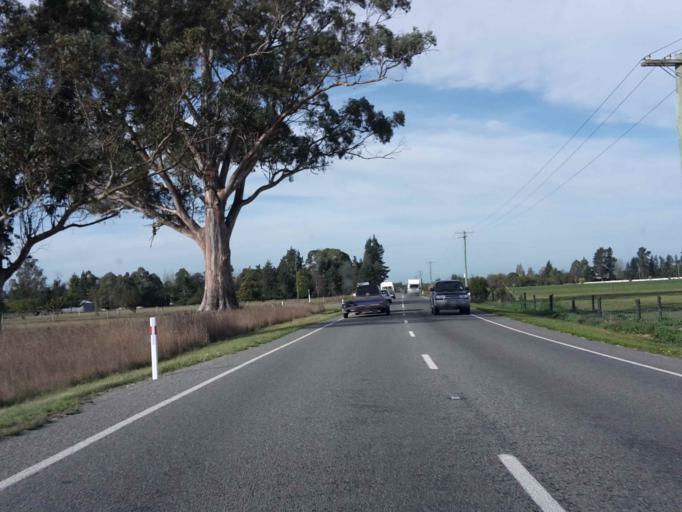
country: NZ
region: Canterbury
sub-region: Timaru District
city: Pleasant Point
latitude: -44.1134
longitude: 171.2164
